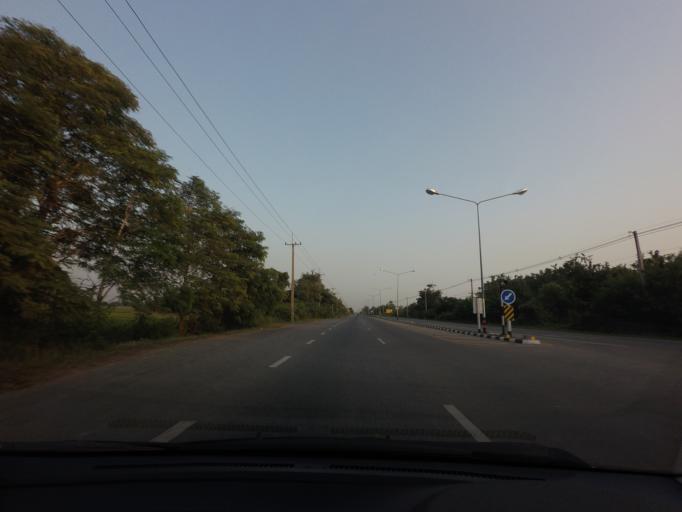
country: TH
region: Sukhothai
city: Kong Krailat
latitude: 17.0140
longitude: 99.9145
